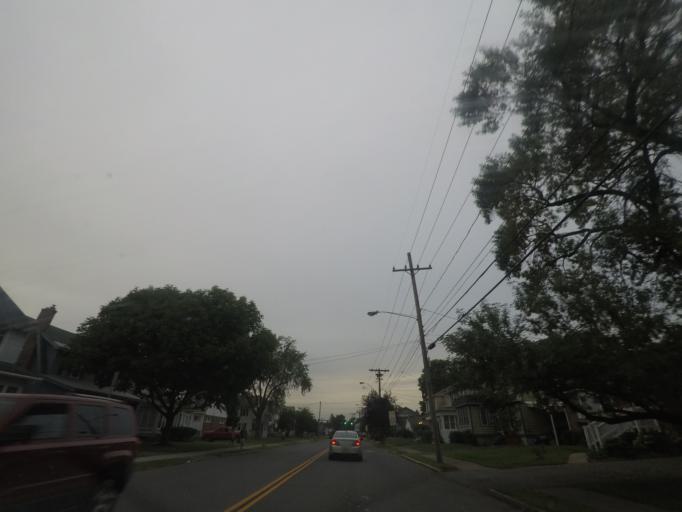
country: US
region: New York
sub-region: Albany County
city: Albany
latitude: 42.6434
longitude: -73.7915
